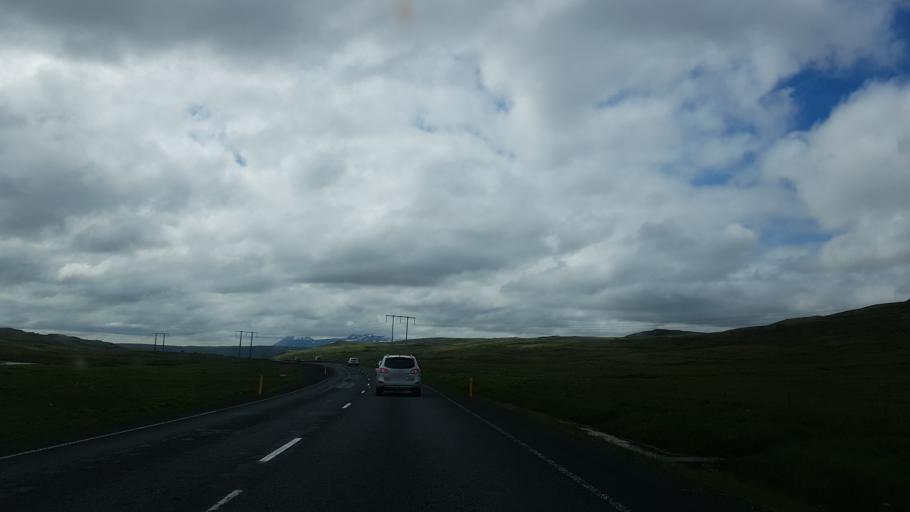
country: IS
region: West
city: Borgarnes
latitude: 64.9317
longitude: -21.0836
